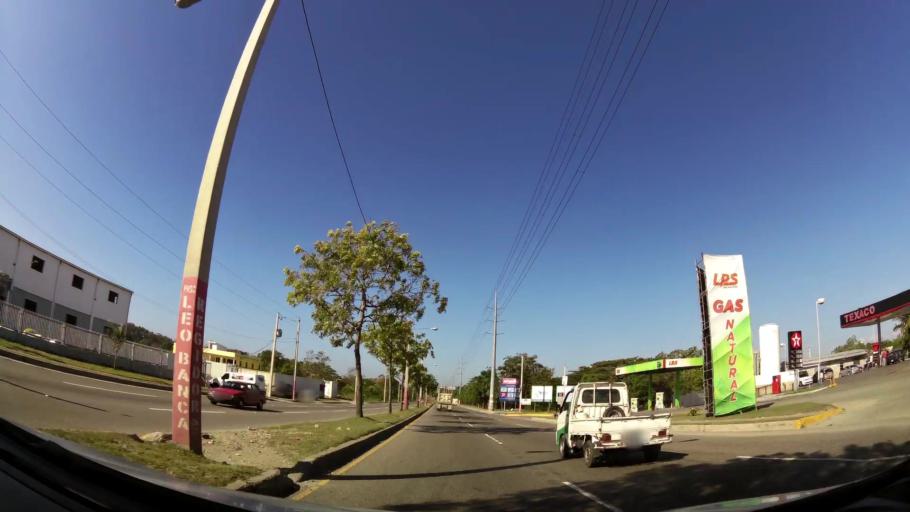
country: DO
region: San Cristobal
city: El Carril
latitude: 18.4485
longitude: -69.9939
